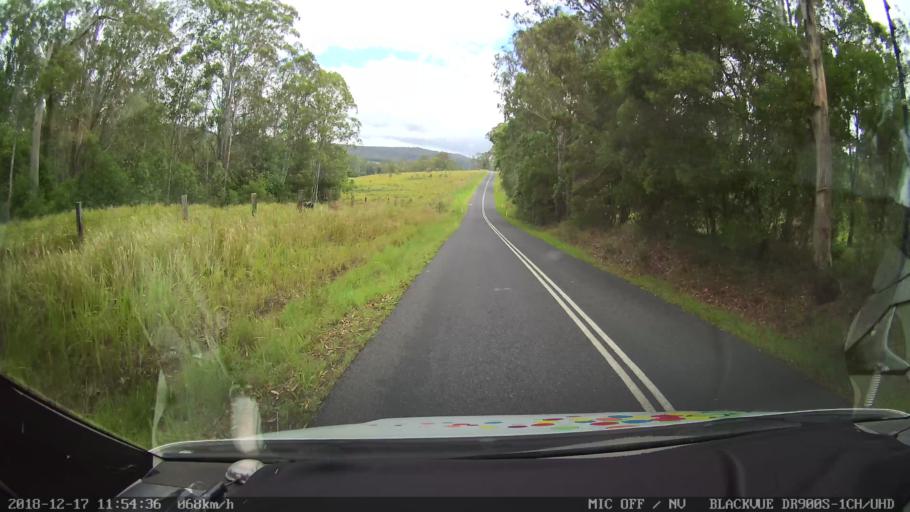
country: AU
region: New South Wales
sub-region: Kyogle
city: Kyogle
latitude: -28.5646
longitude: 152.5826
